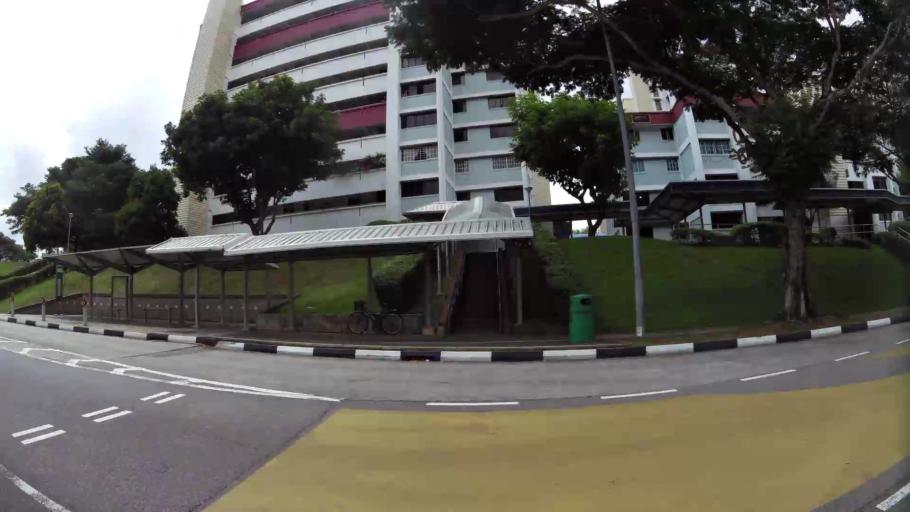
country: MY
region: Johor
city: Johor Bahru
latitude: 1.4366
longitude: 103.7825
